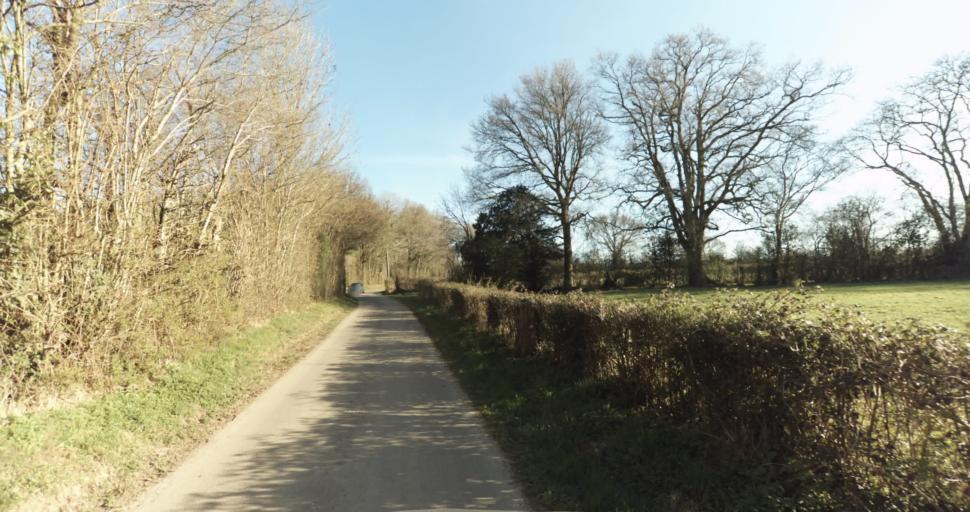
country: FR
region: Lower Normandy
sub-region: Departement du Calvados
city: Livarot
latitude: 48.9864
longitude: 0.0855
